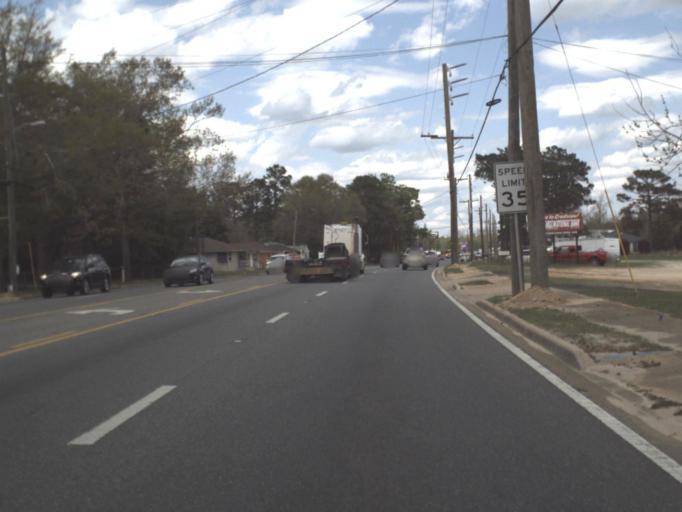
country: US
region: Florida
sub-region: Okaloosa County
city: Crestview
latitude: 30.7748
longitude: -86.5640
